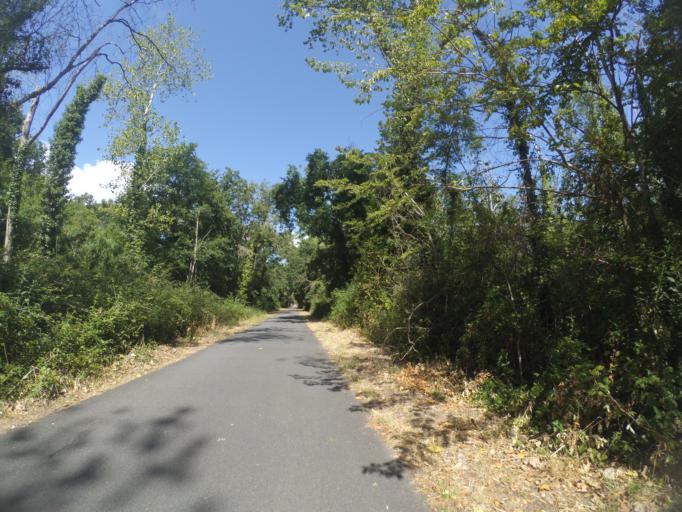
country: FR
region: Poitou-Charentes
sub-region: Departement de la Charente-Maritime
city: Les Mathes
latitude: 45.6787
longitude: -1.1552
